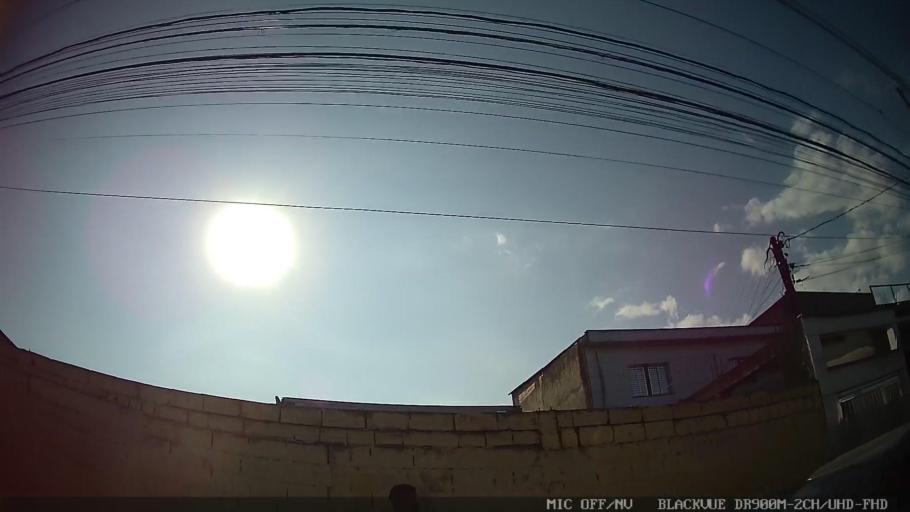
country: BR
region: Sao Paulo
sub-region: Ferraz De Vasconcelos
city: Ferraz de Vasconcelos
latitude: -23.5505
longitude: -46.4131
